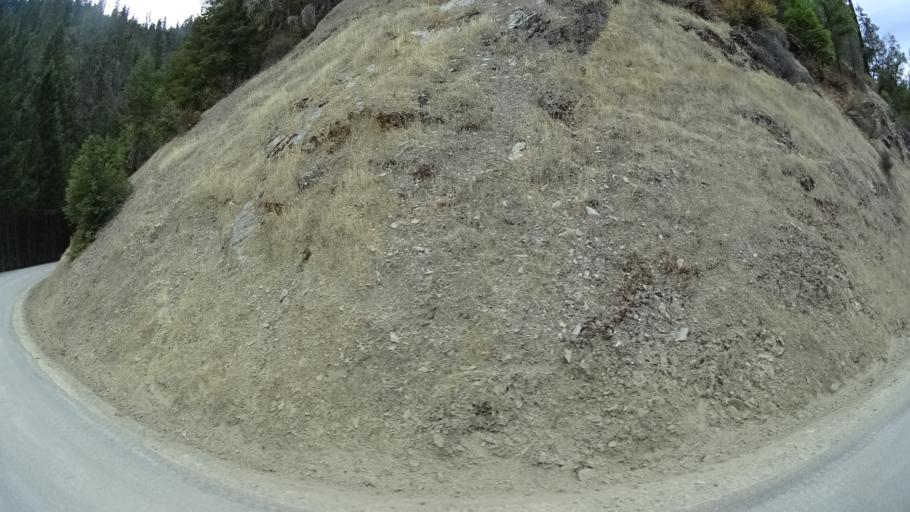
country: US
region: California
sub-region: Siskiyou County
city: Happy Camp
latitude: 41.7727
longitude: -123.3481
